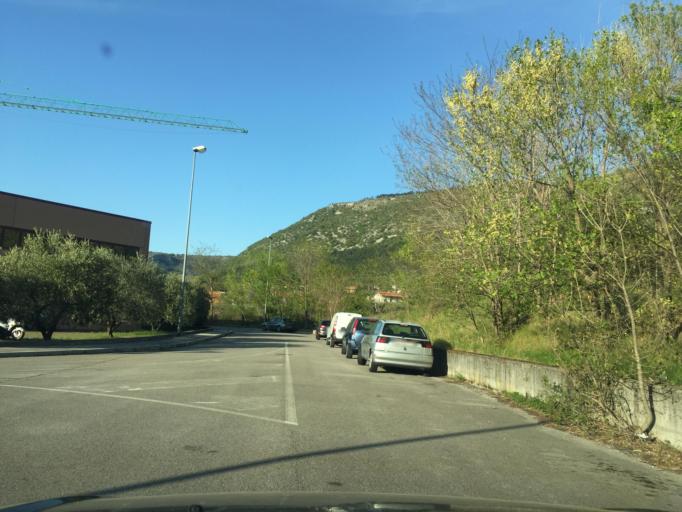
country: IT
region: Friuli Venezia Giulia
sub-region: Provincia di Trieste
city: Dolina
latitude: 45.6011
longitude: 13.8514
